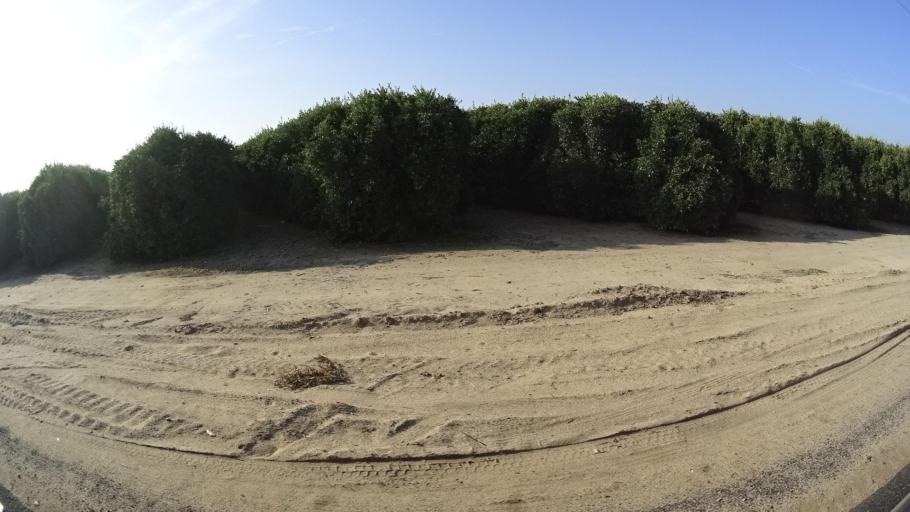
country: US
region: California
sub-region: Kern County
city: McFarland
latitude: 35.6706
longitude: -119.1294
